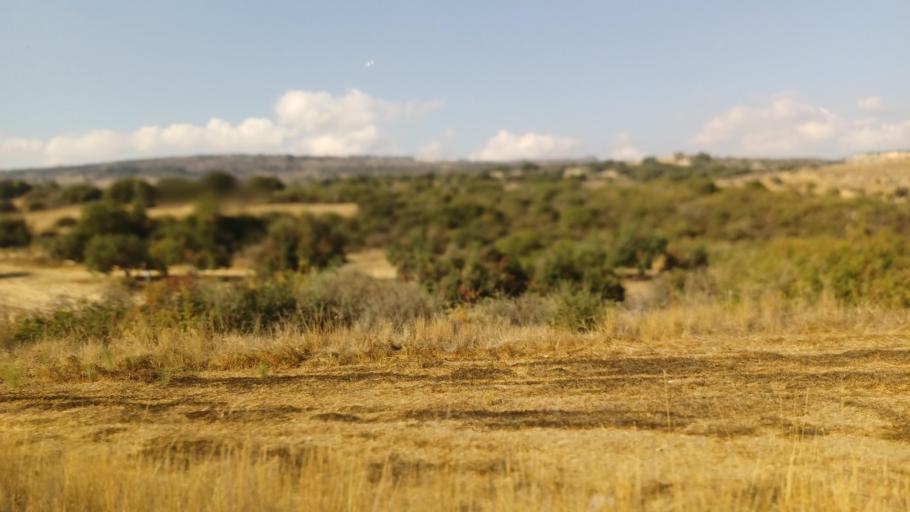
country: CY
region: Pafos
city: Polis
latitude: 34.9793
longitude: 32.4309
